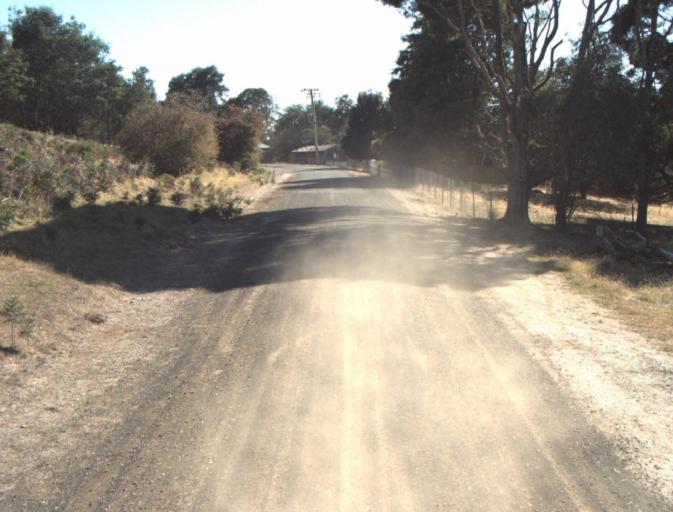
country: AU
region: Tasmania
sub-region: Dorset
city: Scottsdale
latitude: -41.2897
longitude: 147.3595
